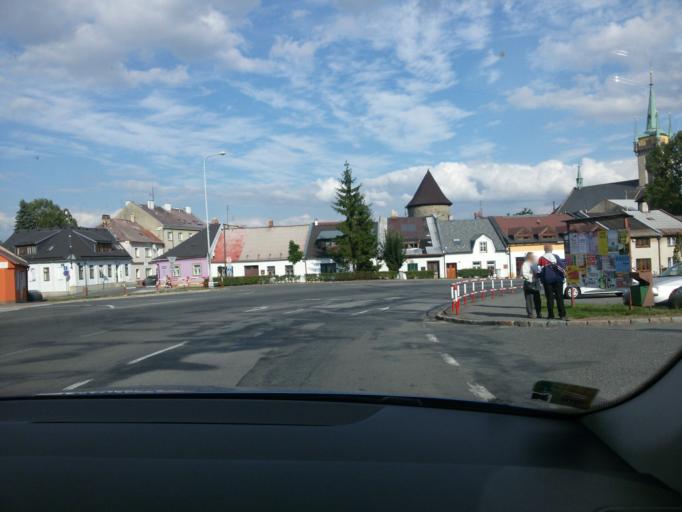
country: CZ
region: Pardubicky
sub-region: Okres Svitavy
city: Policka
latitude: 49.7147
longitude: 16.2608
